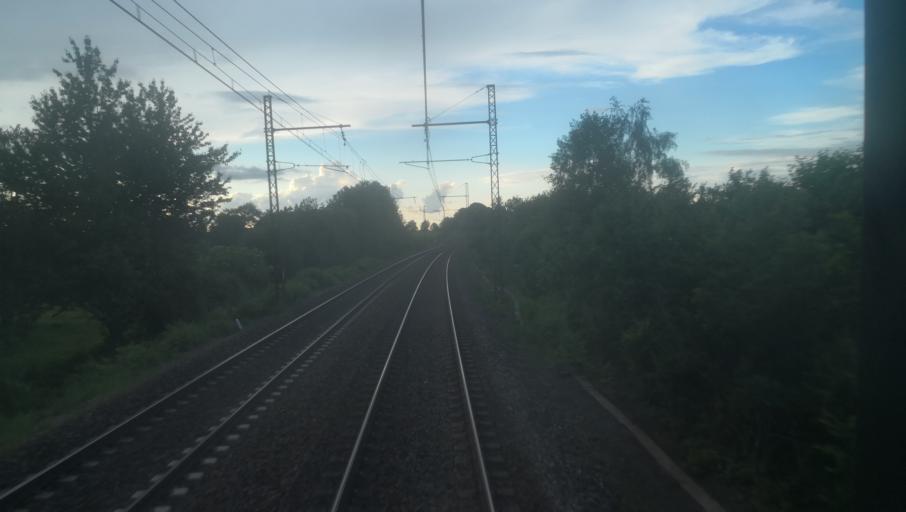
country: FR
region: Limousin
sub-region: Departement de la Creuse
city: La Souterraine
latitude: 46.2600
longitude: 1.4744
